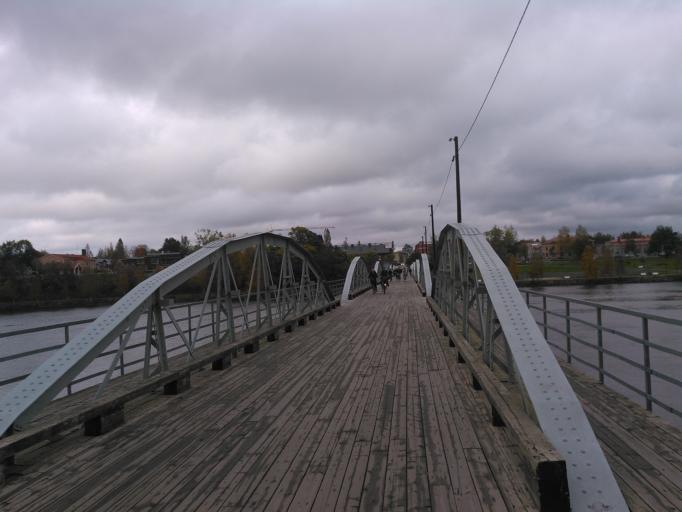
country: SE
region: Vaesterbotten
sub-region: Umea Kommun
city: Umea
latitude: 63.8239
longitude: 20.2485
